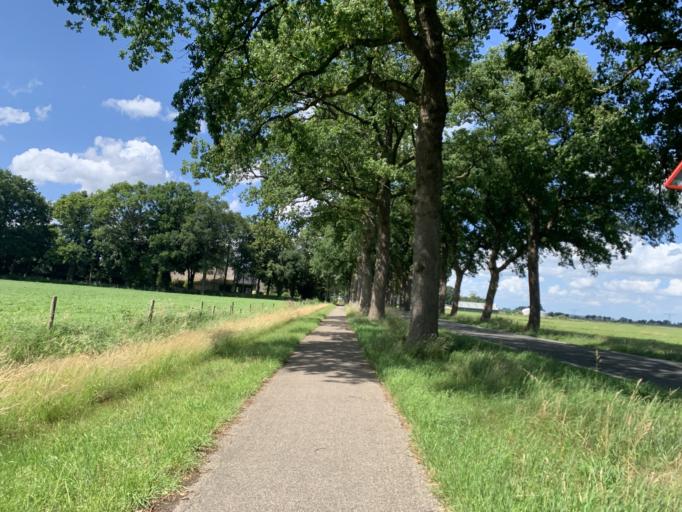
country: NL
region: Drenthe
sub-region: Gemeente Tynaarlo
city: Zuidlaren
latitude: 53.1369
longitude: 6.6538
